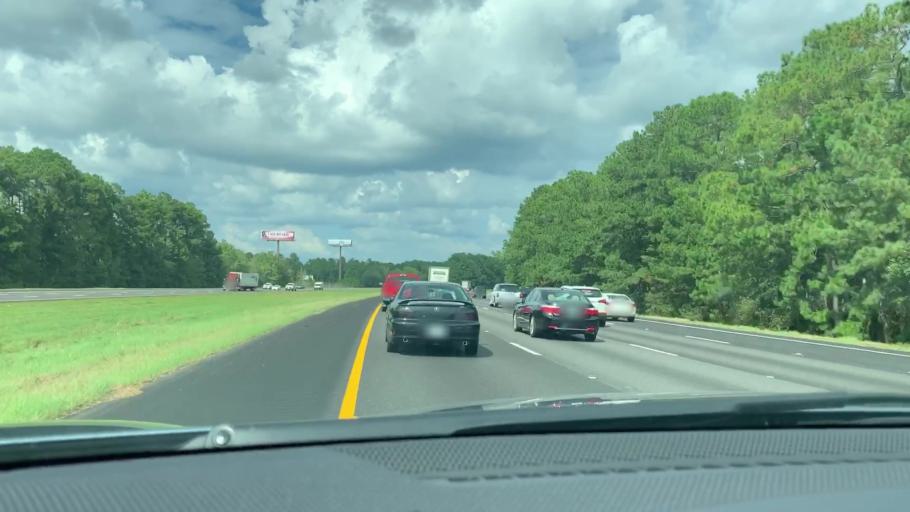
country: US
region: Georgia
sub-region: Chatham County
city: Pooler
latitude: 32.1473
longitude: -81.2402
